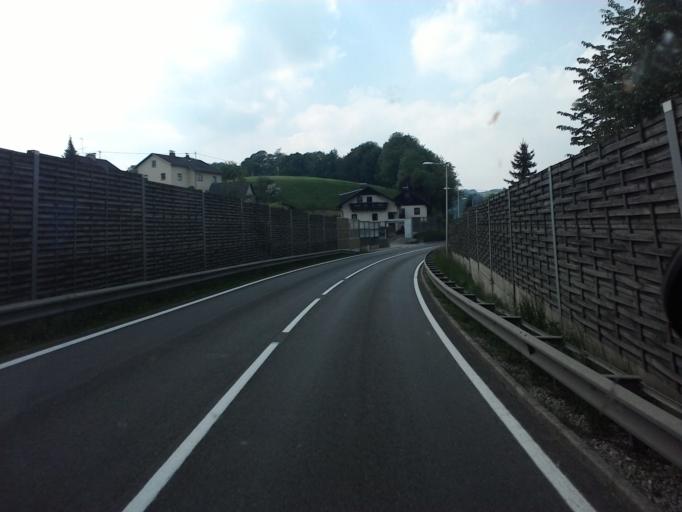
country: AT
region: Upper Austria
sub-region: Politischer Bezirk Kirchdorf an der Krems
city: Kremsmunster
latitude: 48.0528
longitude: 14.1449
